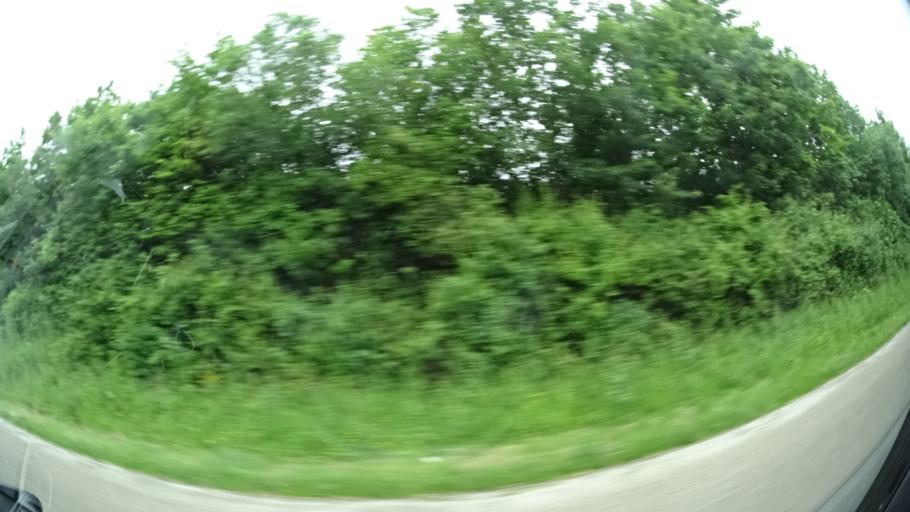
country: DK
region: Central Jutland
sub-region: Arhus Kommune
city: Logten
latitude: 56.2688
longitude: 10.3297
